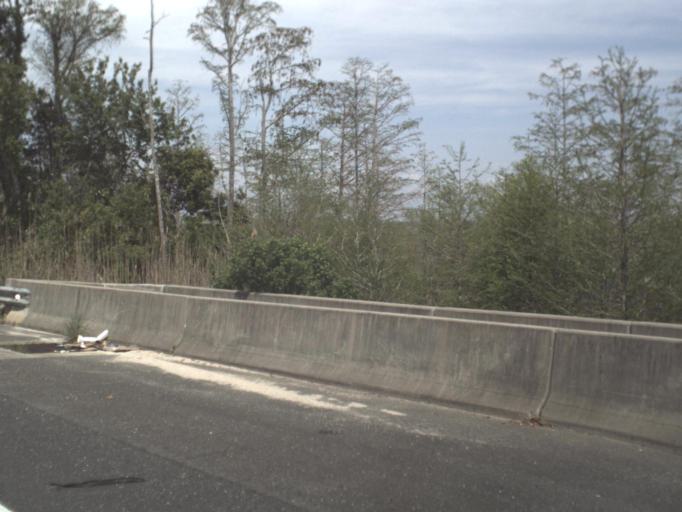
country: US
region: Florida
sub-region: Escambia County
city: Ferry Pass
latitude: 30.5532
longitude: -87.1934
